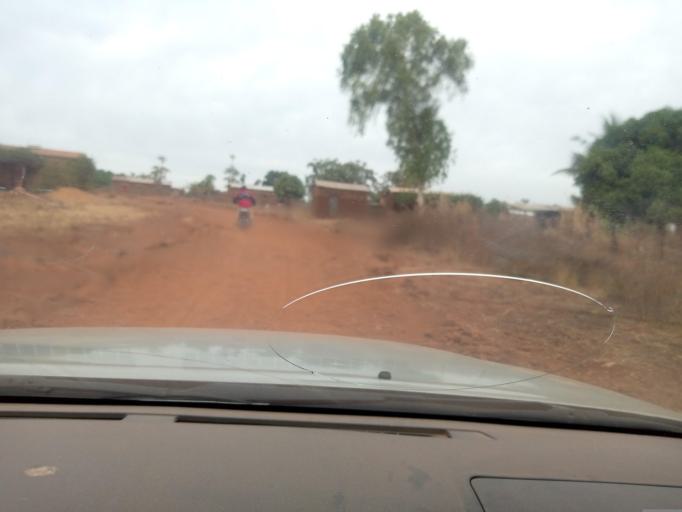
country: ML
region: Sikasso
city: Sikasso
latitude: 11.0199
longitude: -5.7138
